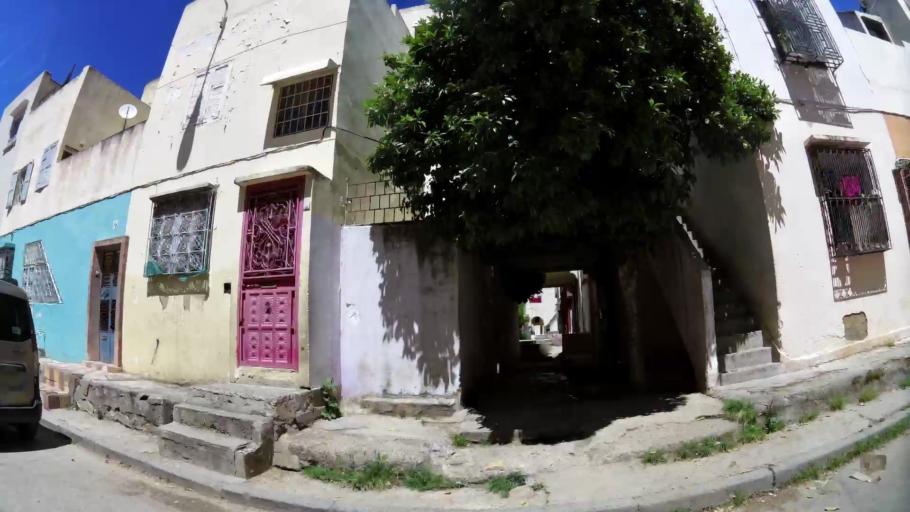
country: MA
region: Meknes-Tafilalet
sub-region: Meknes
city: Meknes
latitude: 33.9012
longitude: -5.5757
